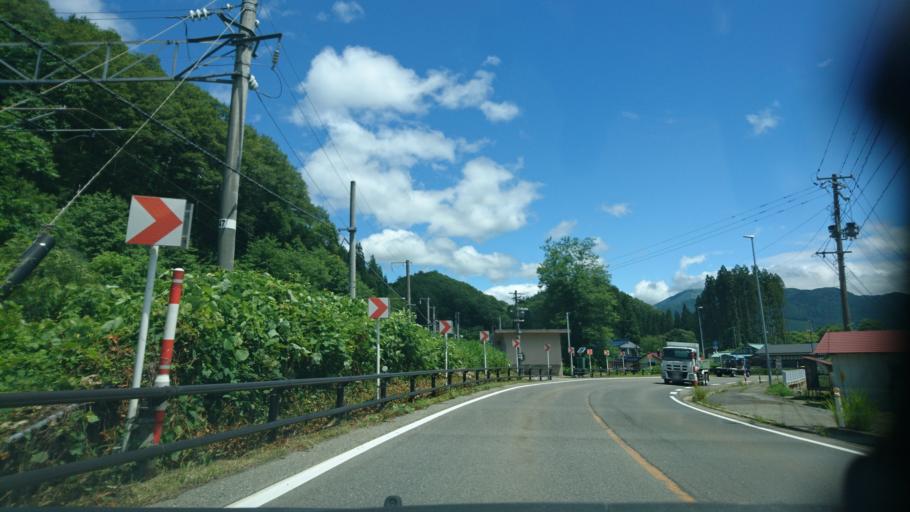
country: JP
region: Akita
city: Kakunodatemachi
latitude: 39.6811
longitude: 140.7038
